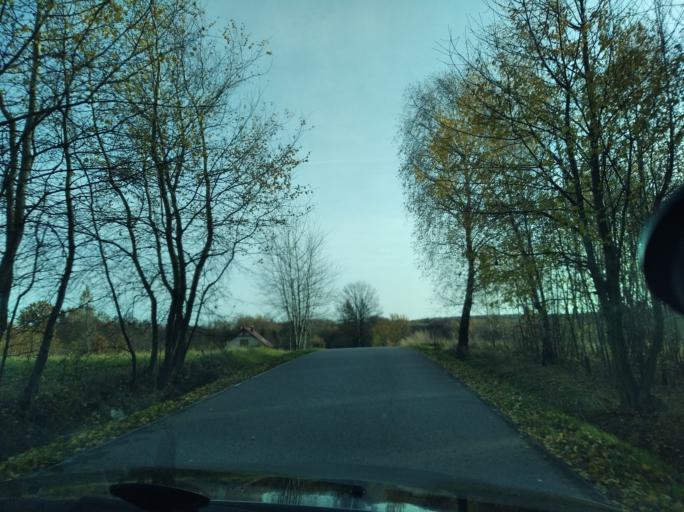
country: PL
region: Subcarpathian Voivodeship
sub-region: Powiat rzeszowski
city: Siedliska
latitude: 49.9345
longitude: 21.9624
